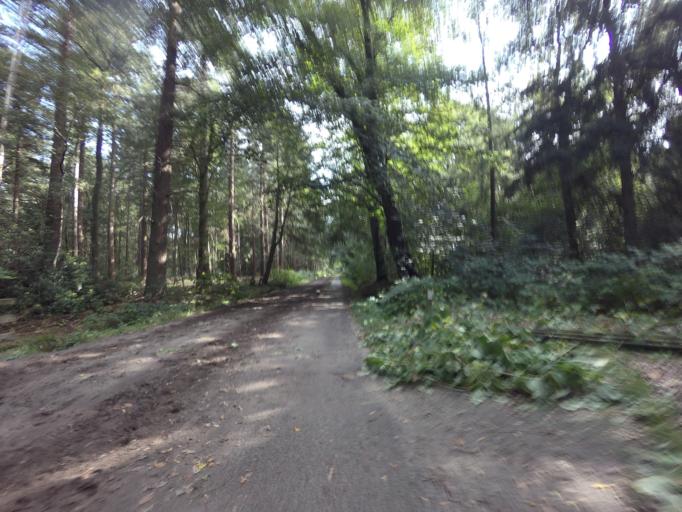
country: NL
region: Overijssel
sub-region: Gemeente Enschede
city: Enschede
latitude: 52.2571
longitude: 6.8550
